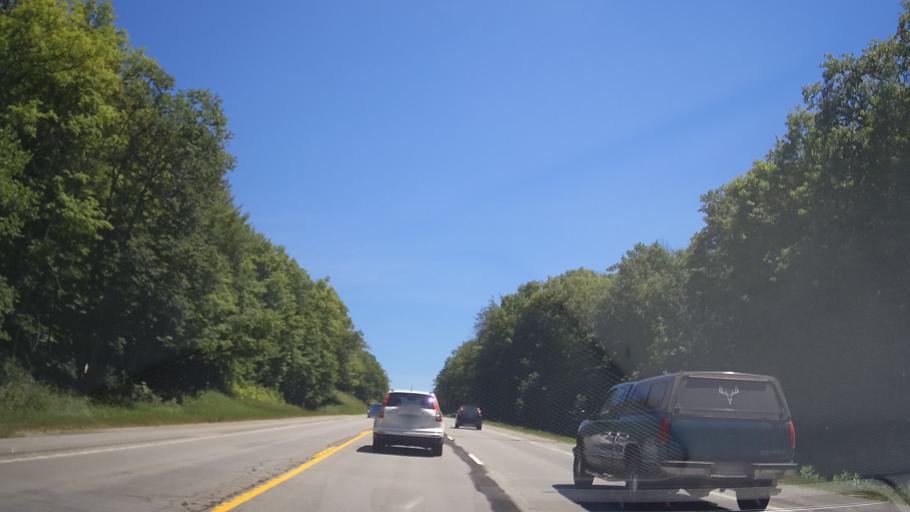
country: US
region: Michigan
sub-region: Wexford County
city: Manton
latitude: 44.3430
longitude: -85.5995
